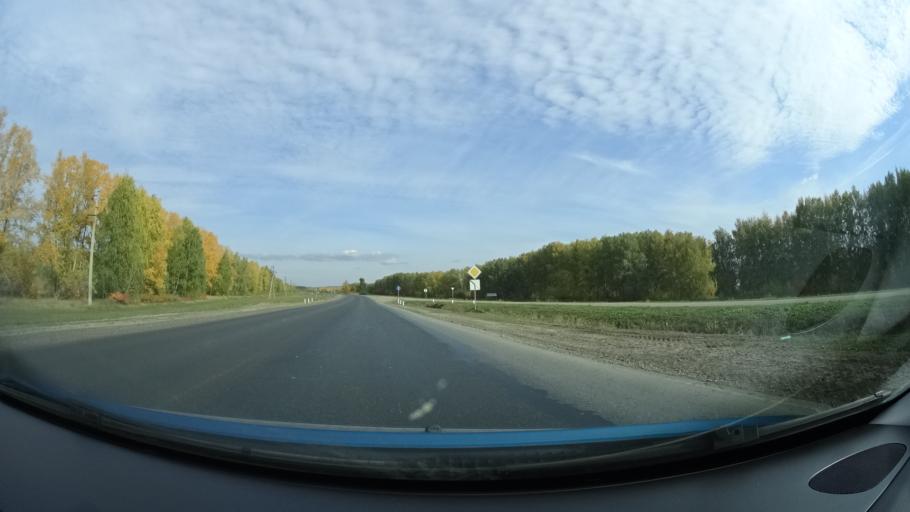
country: RU
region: Bashkortostan
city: Kandry
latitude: 54.5144
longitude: 54.0323
